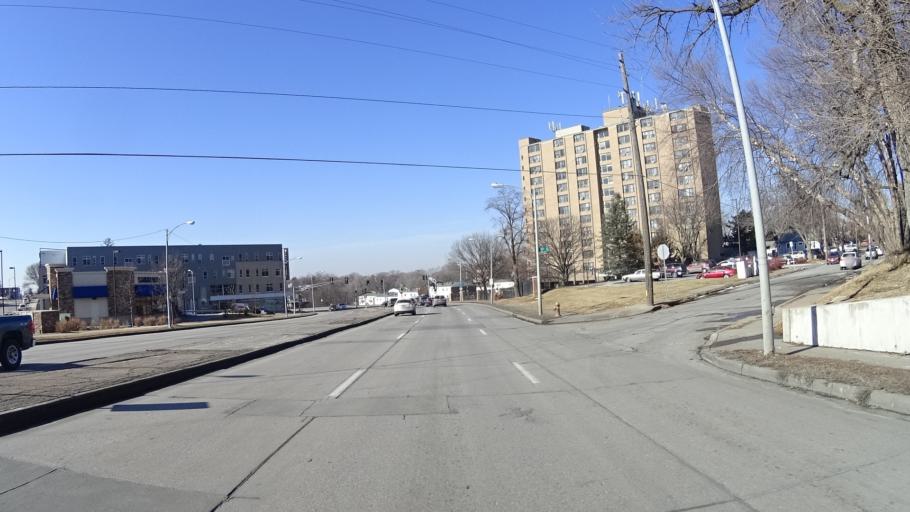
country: US
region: Nebraska
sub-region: Douglas County
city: Omaha
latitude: 41.2860
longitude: -96.0034
